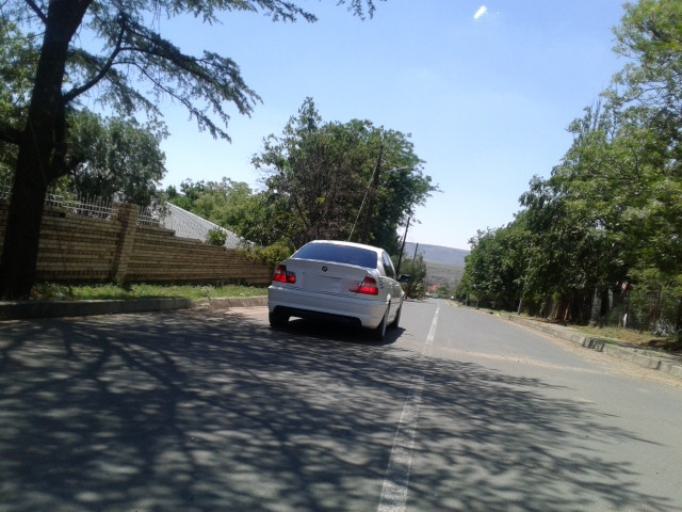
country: LS
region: Maseru
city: Maseru
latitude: -29.3050
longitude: 27.4681
